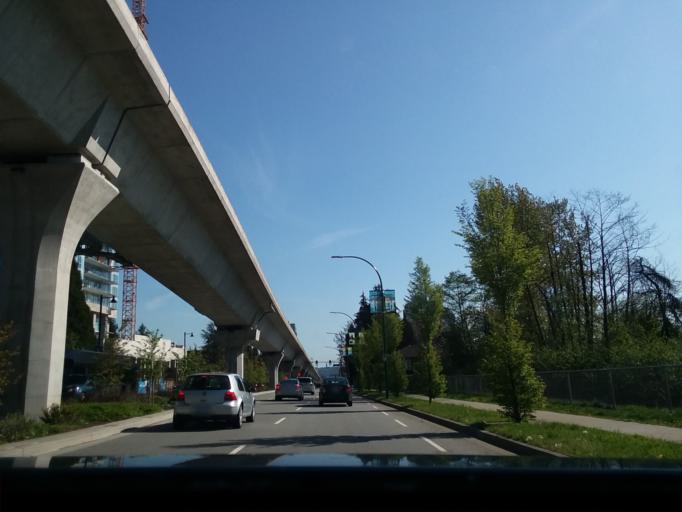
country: CA
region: British Columbia
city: Port Moody
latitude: 49.2581
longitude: -122.8932
